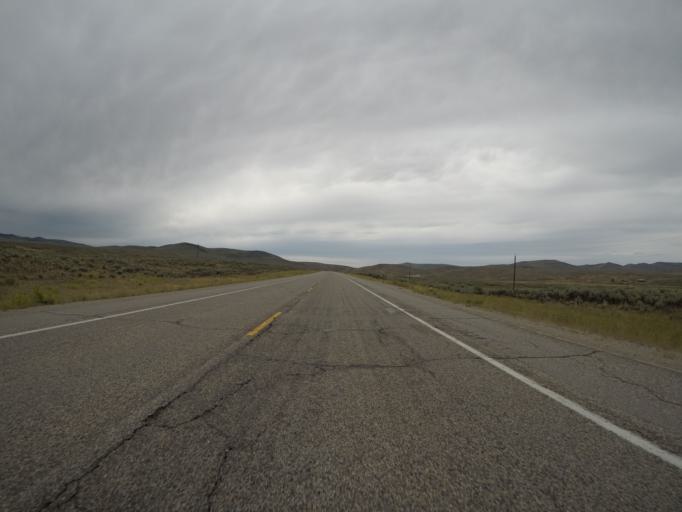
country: US
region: Wyoming
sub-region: Lincoln County
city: Kemmerer
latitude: 41.8166
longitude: -110.7683
